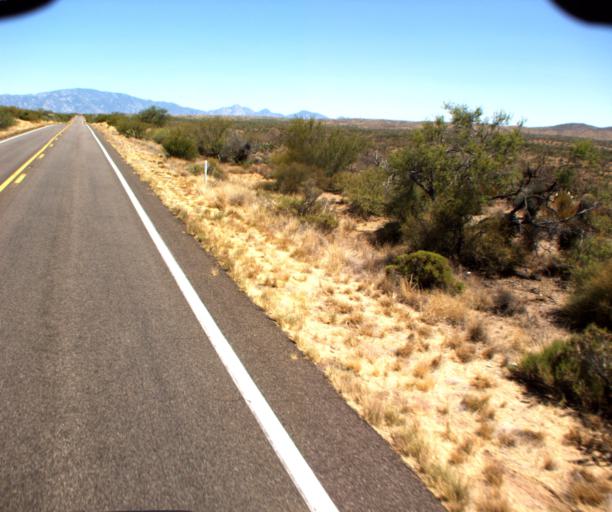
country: US
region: Arizona
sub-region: Pima County
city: Catalina
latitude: 32.6447
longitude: -111.0191
